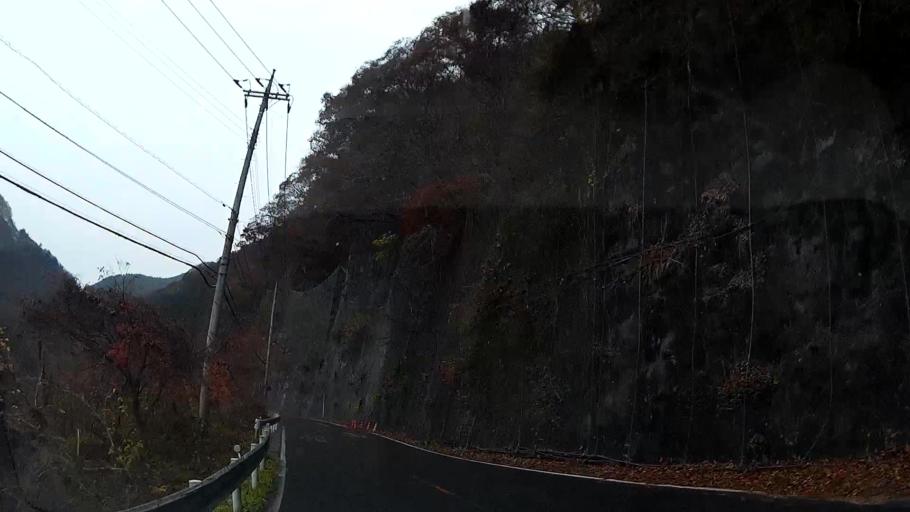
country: JP
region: Saitama
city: Chichibu
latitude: 35.9466
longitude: 138.9238
